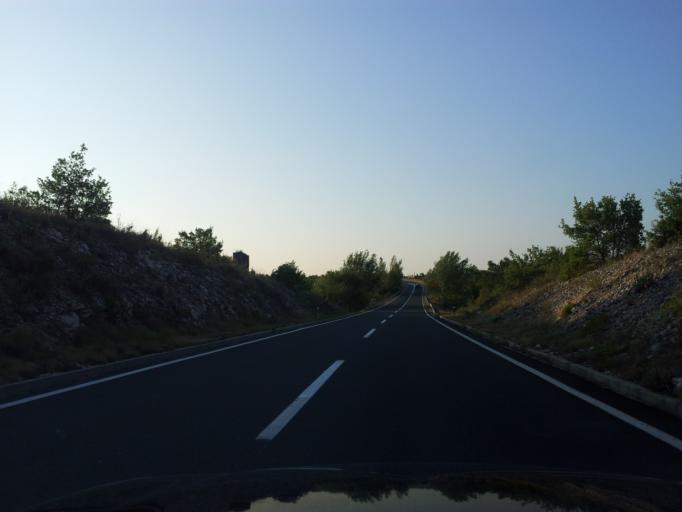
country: HR
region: Zadarska
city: Benkovac
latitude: 44.0102
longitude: 15.5749
